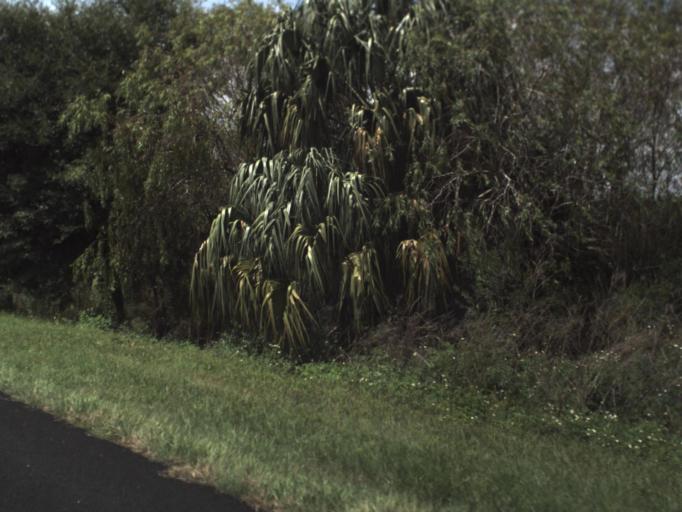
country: US
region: Florida
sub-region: Polk County
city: Dundee
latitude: 27.9789
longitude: -81.6363
